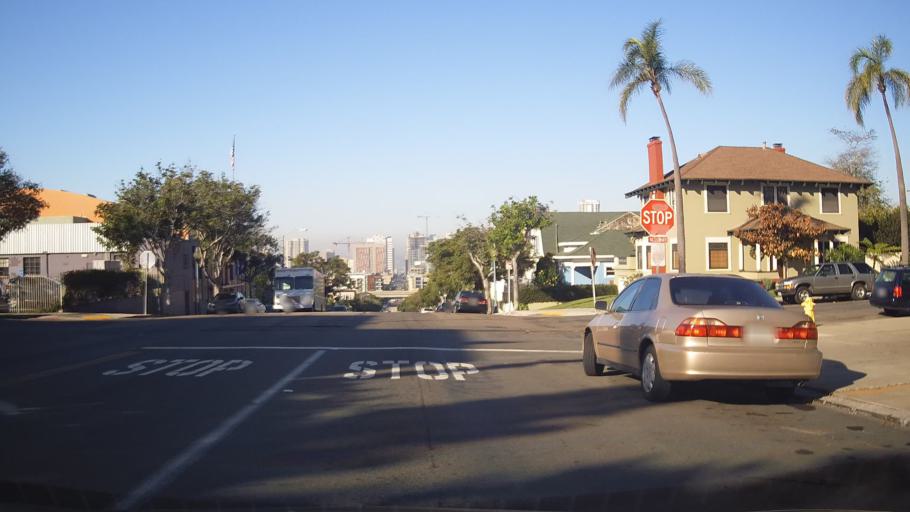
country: US
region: California
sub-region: San Diego County
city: San Diego
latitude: 32.7159
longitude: -117.1421
